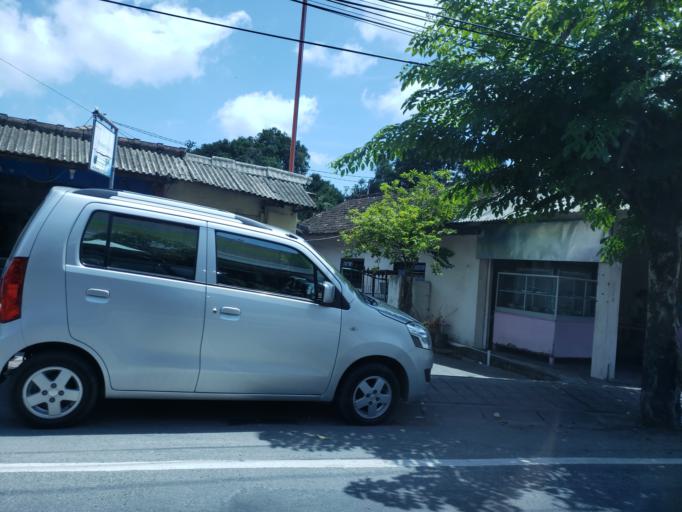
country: ID
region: Bali
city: Jimbaran
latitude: -8.7778
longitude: 115.1700
